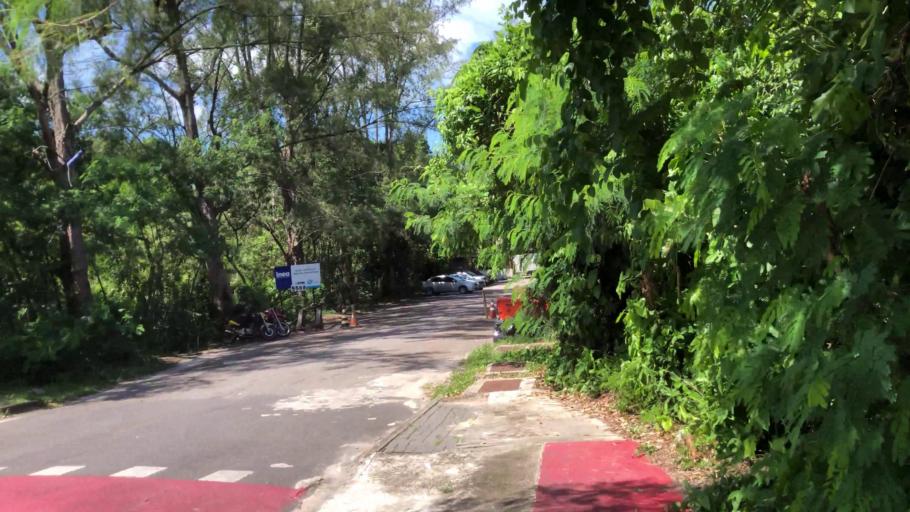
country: BR
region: Rio de Janeiro
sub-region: Nilopolis
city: Nilopolis
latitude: -22.9734
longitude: -43.3987
